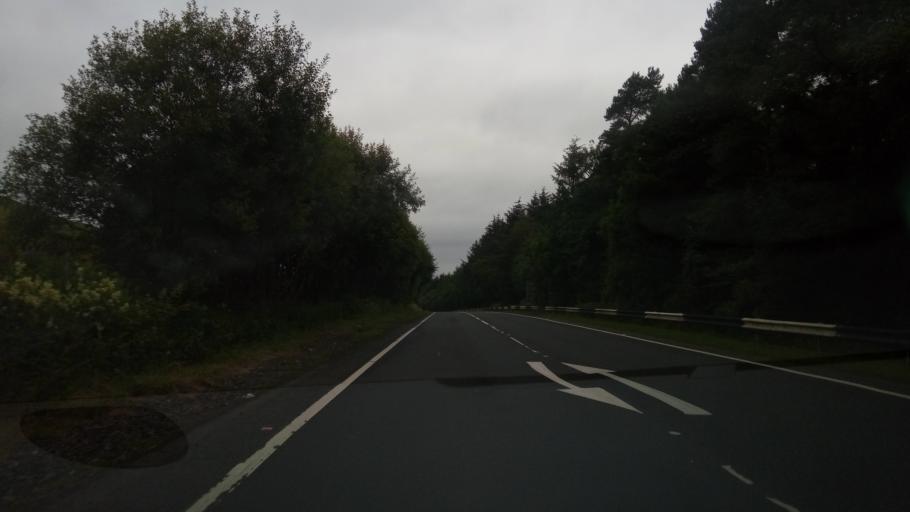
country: GB
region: Scotland
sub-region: The Scottish Borders
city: Hawick
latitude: 55.3591
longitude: -2.8960
